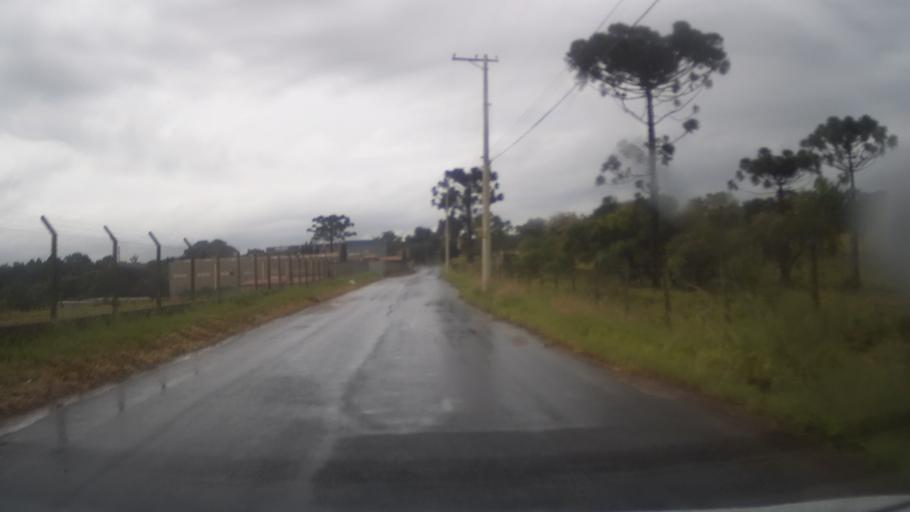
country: BR
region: Sao Paulo
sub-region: Itupeva
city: Itupeva
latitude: -23.1673
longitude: -47.0336
